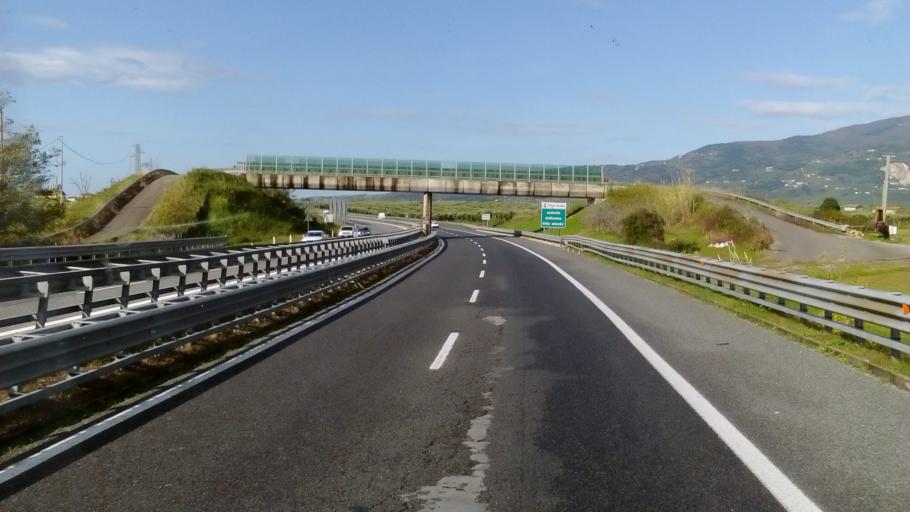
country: IT
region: Calabria
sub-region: Provincia di Catanzaro
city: Santa Eufemia Lamezia
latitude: 38.9224
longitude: 16.2611
